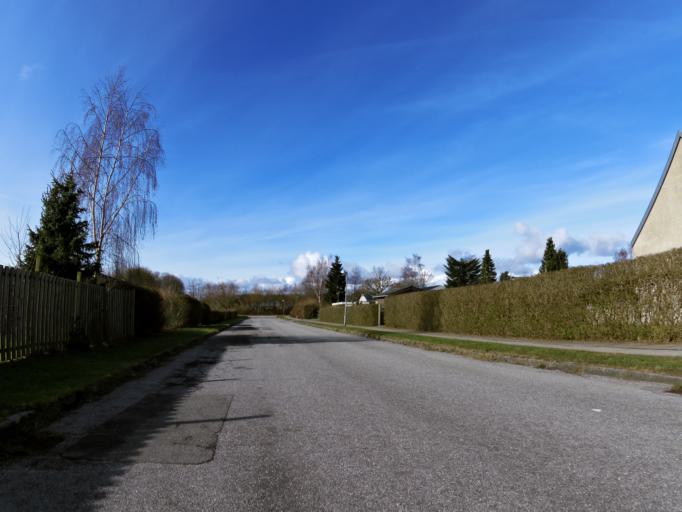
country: DK
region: Central Jutland
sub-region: Arhus Kommune
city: Tranbjerg
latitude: 56.0916
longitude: 10.1194
